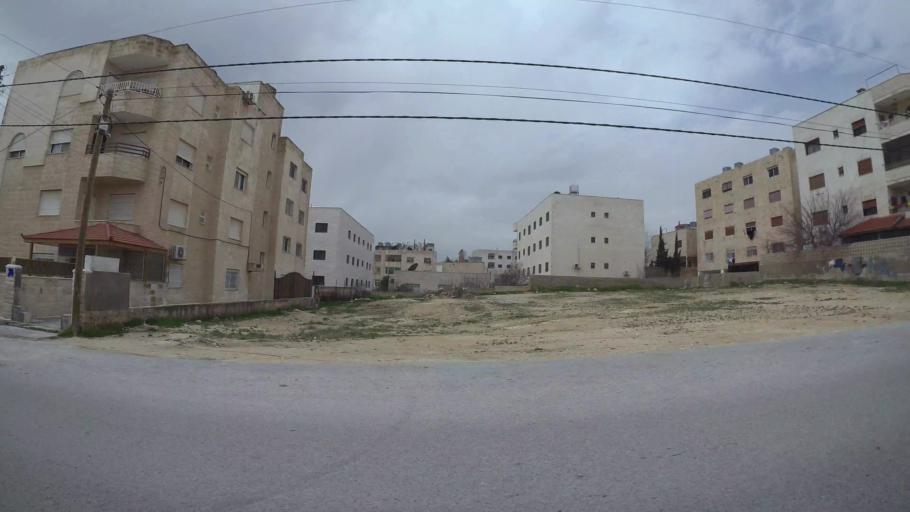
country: JO
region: Amman
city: Umm as Summaq
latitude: 31.9046
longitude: 35.8433
